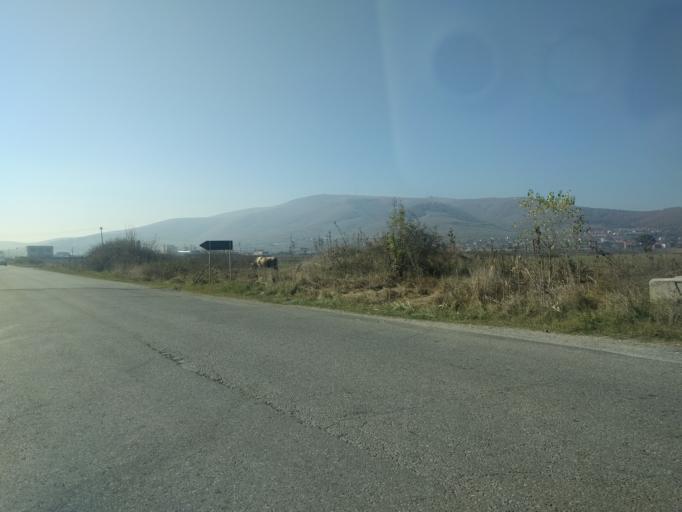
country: XK
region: Pristina
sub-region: Komuna e Gracanices
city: Glanica
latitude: 42.5875
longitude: 21.0170
